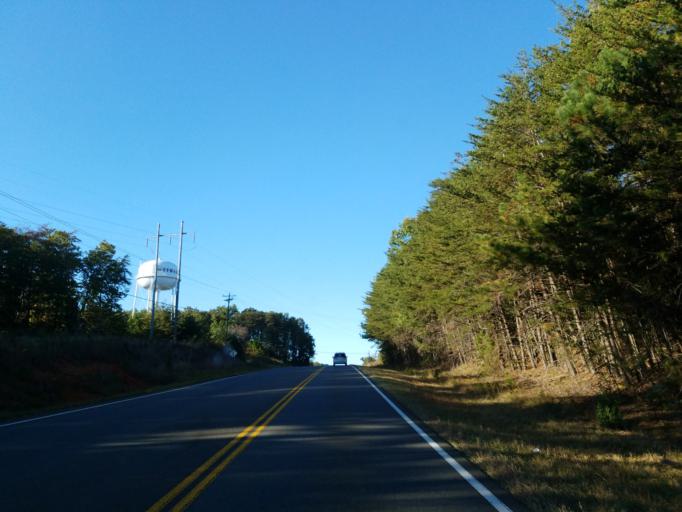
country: US
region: Georgia
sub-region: Pickens County
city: Nelson
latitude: 34.3975
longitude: -84.3825
